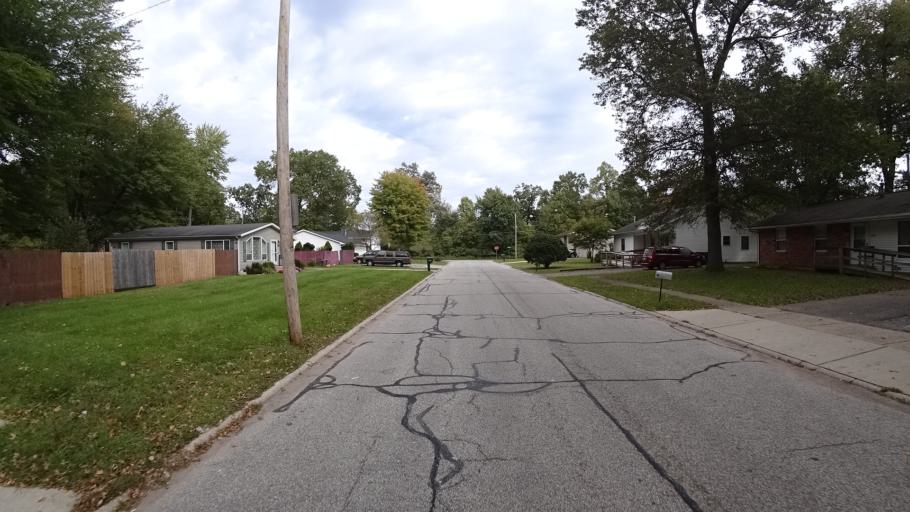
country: US
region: Indiana
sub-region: LaPorte County
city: Trail Creek
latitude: 41.6976
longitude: -86.8685
